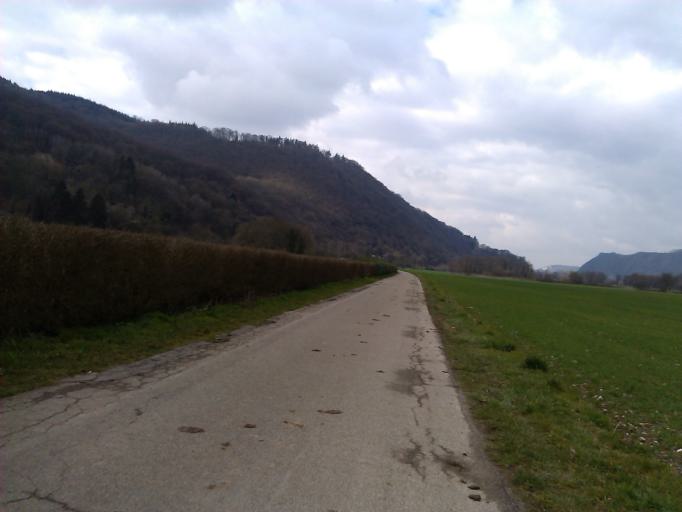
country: DE
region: Rheinland-Pfalz
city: Hammerstein
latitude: 50.4584
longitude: 7.3553
